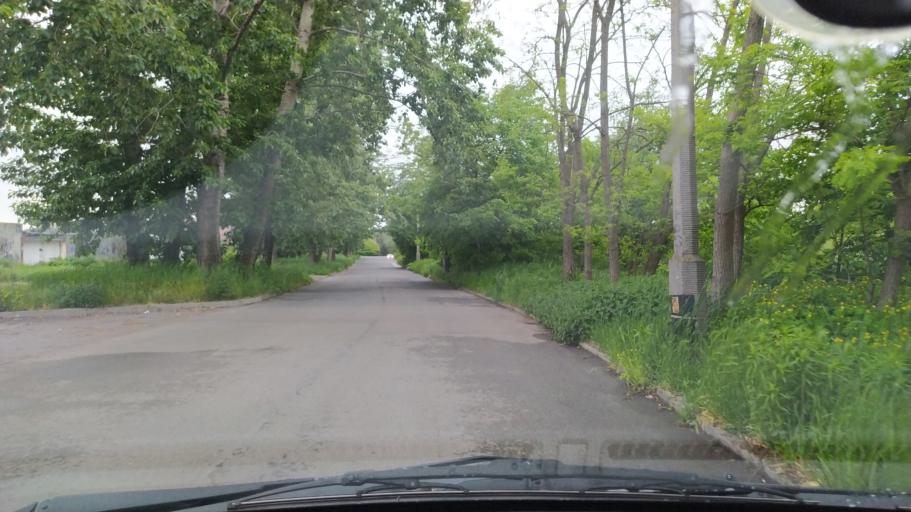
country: PL
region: Silesian Voivodeship
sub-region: Powiat gliwicki
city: Przyszowice
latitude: 50.2956
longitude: 18.7293
